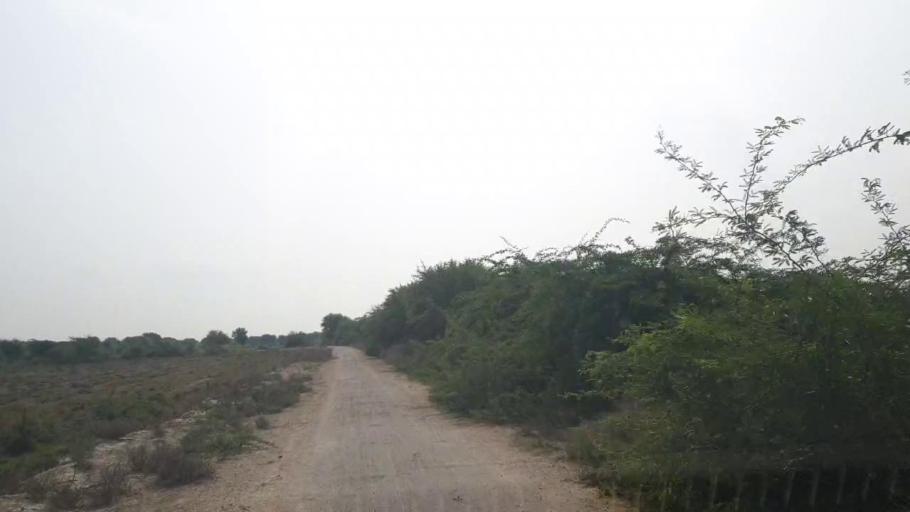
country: PK
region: Sindh
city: Badin
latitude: 24.5490
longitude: 68.6877
